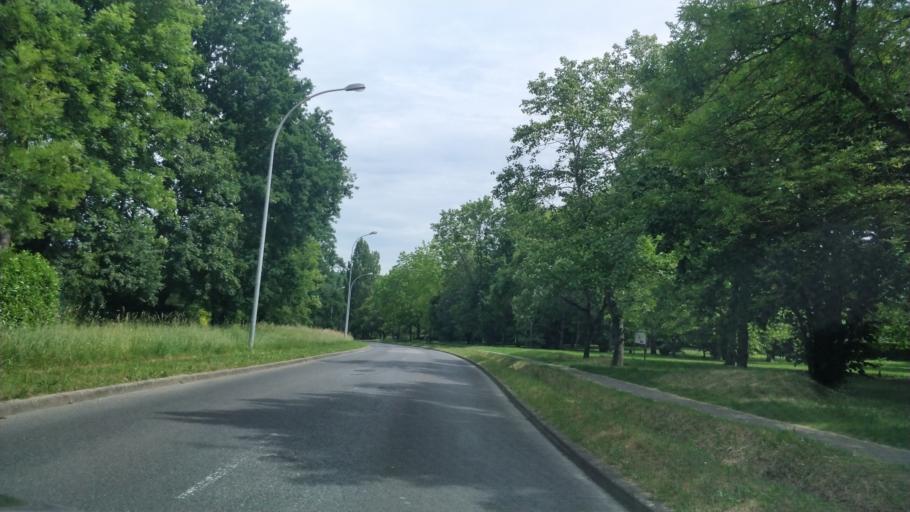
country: FR
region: Ile-de-France
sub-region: Departement de l'Essonne
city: Limours
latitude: 48.6401
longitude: 2.0797
